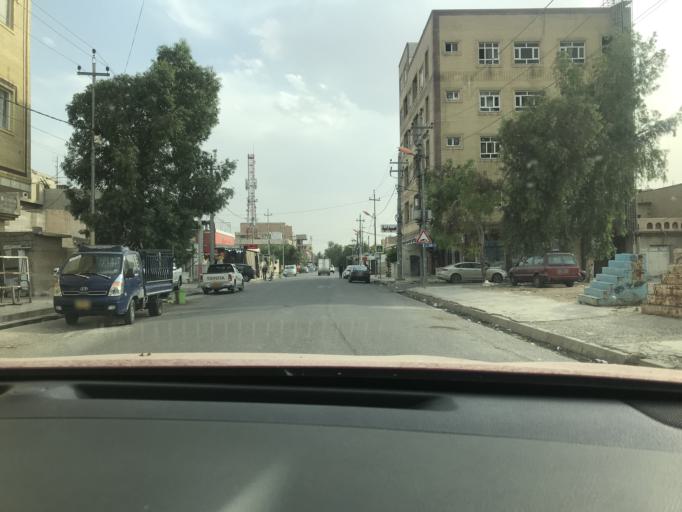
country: IQ
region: Arbil
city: Erbil
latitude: 36.1789
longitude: 43.9774
